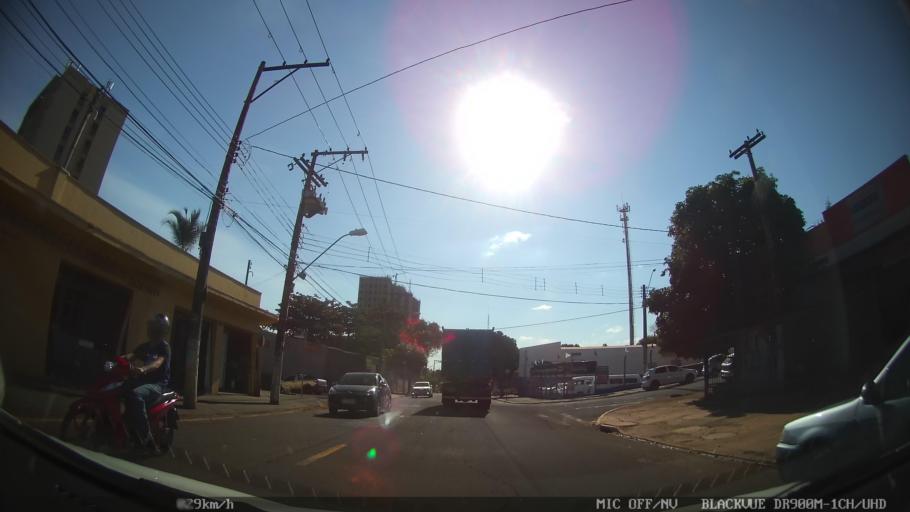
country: BR
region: Sao Paulo
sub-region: Ribeirao Preto
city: Ribeirao Preto
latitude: -21.1793
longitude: -47.7770
